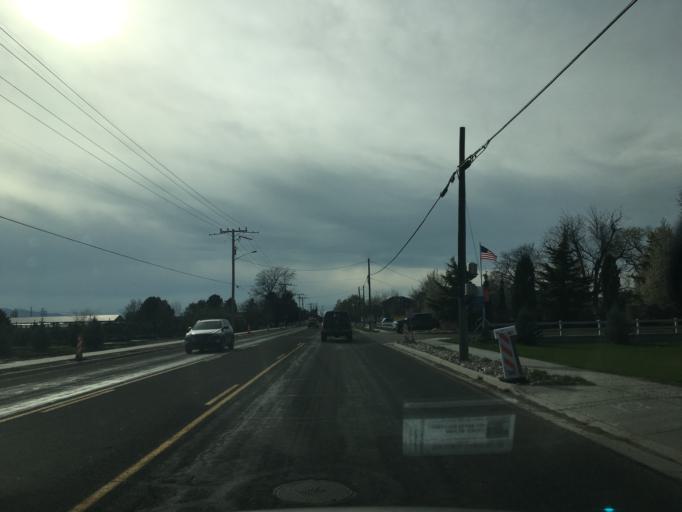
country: US
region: Utah
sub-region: Davis County
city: Layton
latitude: 41.0602
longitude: -111.9954
